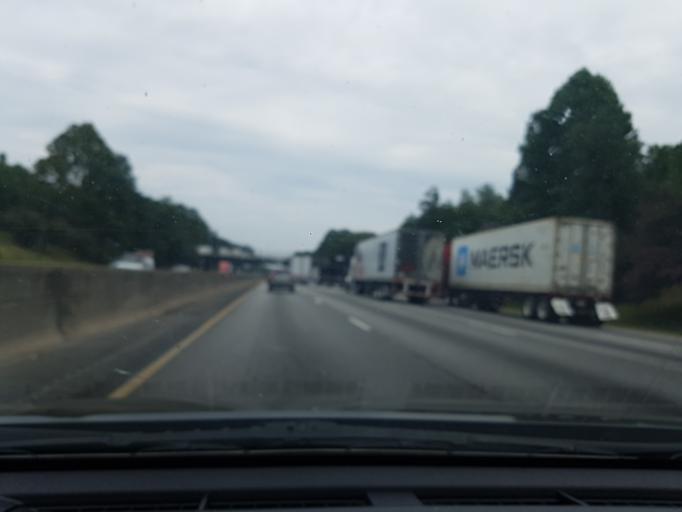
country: US
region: Georgia
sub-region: DeKalb County
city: Gresham Park
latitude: 33.6827
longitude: -84.3116
